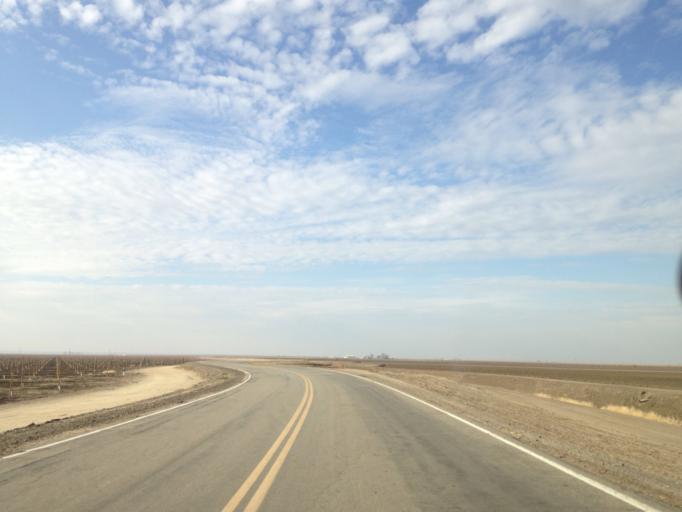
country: US
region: California
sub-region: Kern County
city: Buttonwillow
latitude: 35.4429
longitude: -119.5511
